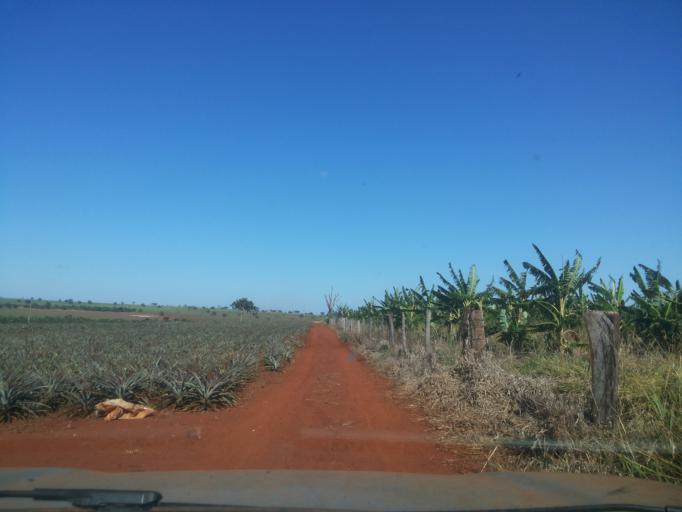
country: BR
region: Minas Gerais
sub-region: Centralina
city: Centralina
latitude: -18.7623
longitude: -49.2024
